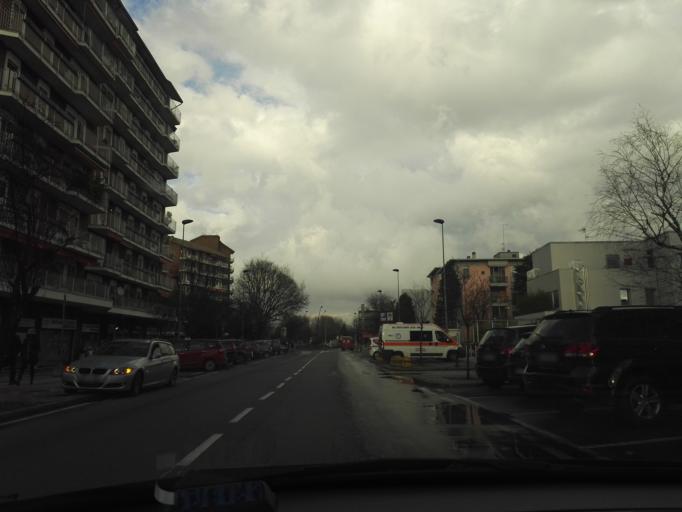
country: IT
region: Lombardy
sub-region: Citta metropolitana di Milano
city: San Donato Milanese
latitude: 45.4114
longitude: 9.2744
